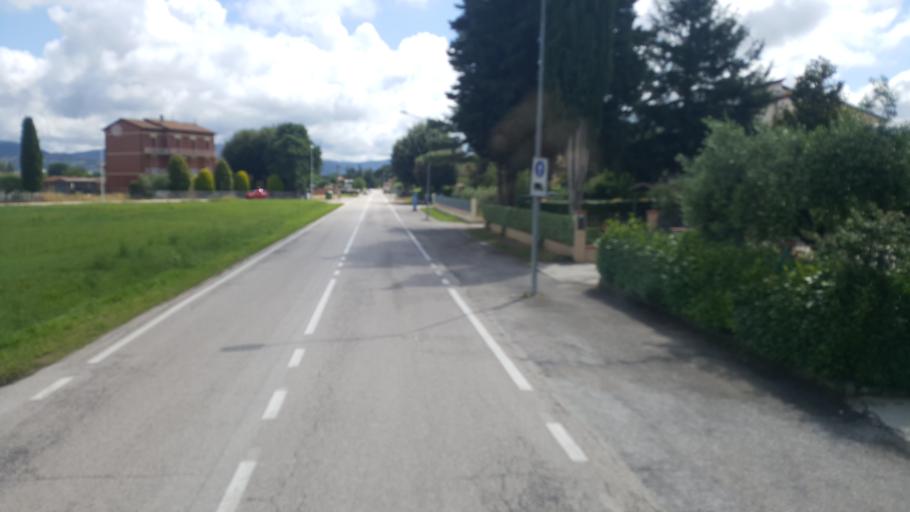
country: IT
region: Umbria
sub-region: Provincia di Perugia
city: Bastia umbra
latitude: 43.0648
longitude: 12.5258
